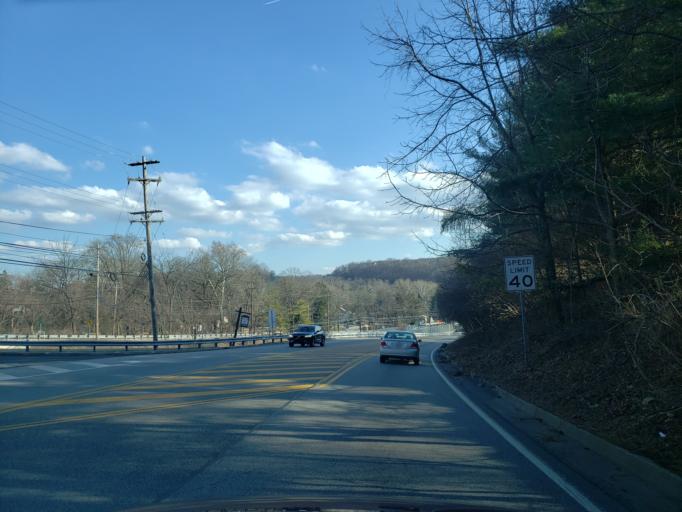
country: US
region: Pennsylvania
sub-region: Montgomery County
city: West Conshohocken
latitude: 40.0729
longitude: -75.3442
